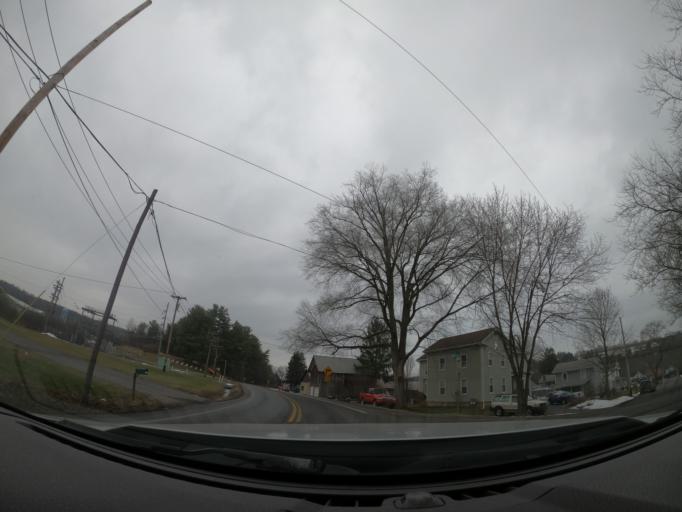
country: US
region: New York
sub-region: Cayuga County
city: Moravia
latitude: 42.6588
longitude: -76.4327
